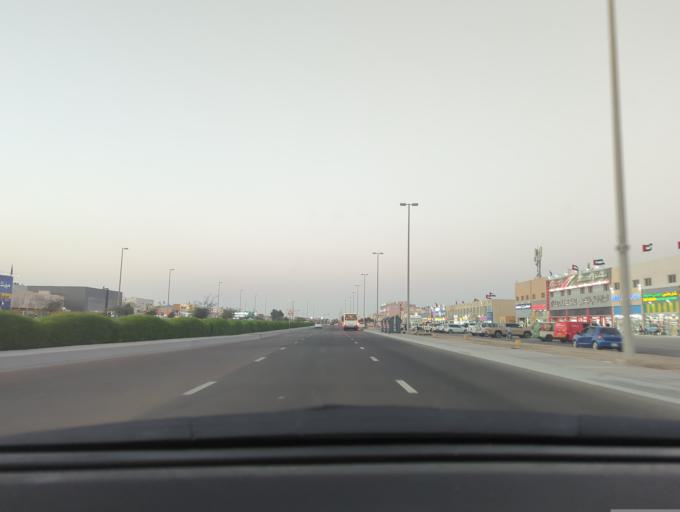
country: AE
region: Abu Dhabi
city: Abu Dhabi
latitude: 24.3743
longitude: 54.5161
